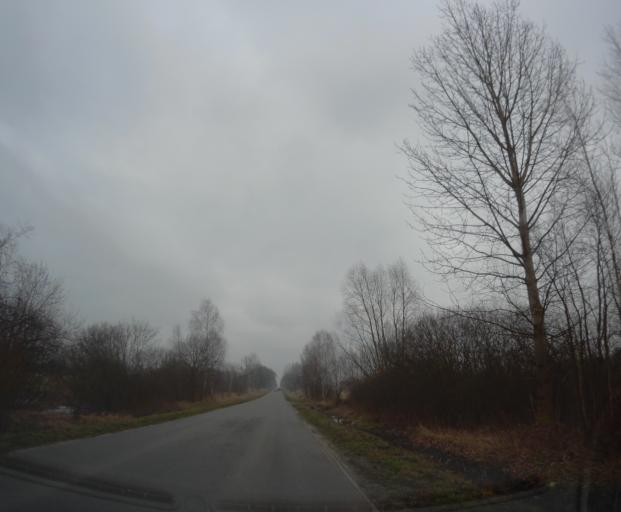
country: PL
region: Lublin Voivodeship
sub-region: Powiat bilgorajski
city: Bilgoraj
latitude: 50.5393
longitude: 22.6787
